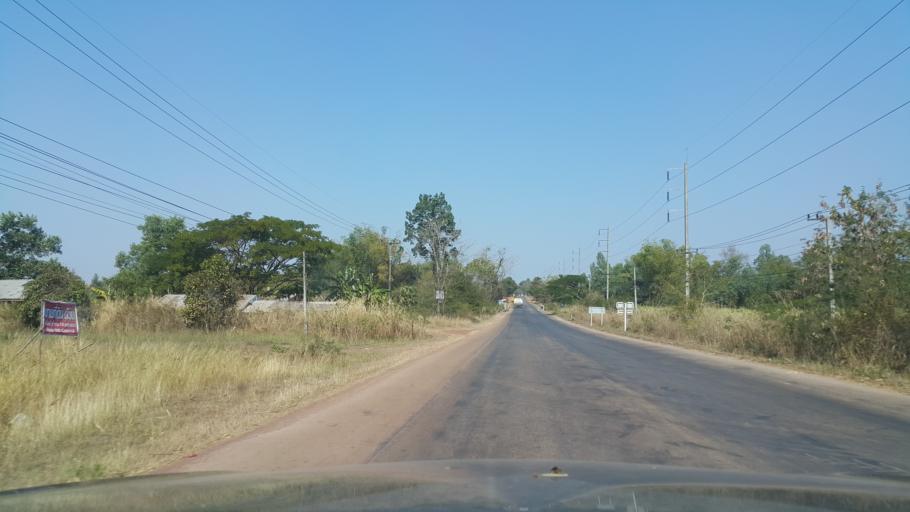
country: TH
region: Changwat Udon Thani
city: Ban Dung
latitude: 17.5968
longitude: 103.2459
